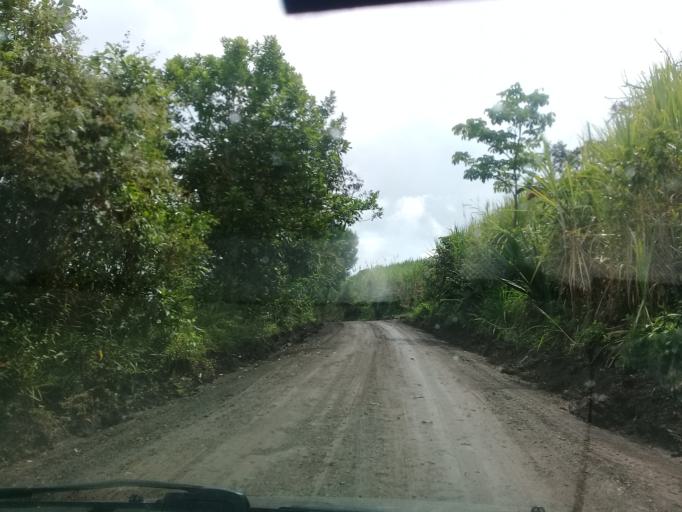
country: CO
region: Cundinamarca
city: Quipile
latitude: 4.7101
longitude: -74.5313
